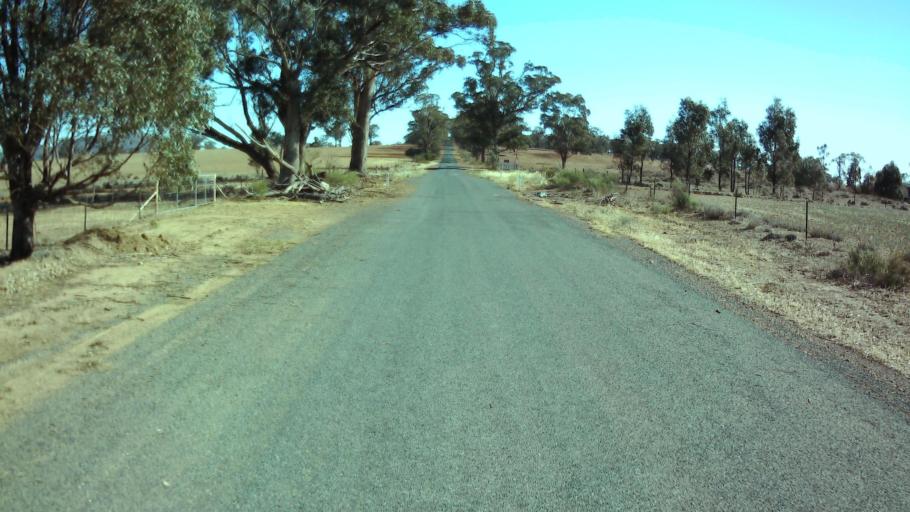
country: AU
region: New South Wales
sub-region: Weddin
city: Grenfell
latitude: -33.7925
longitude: 147.9572
